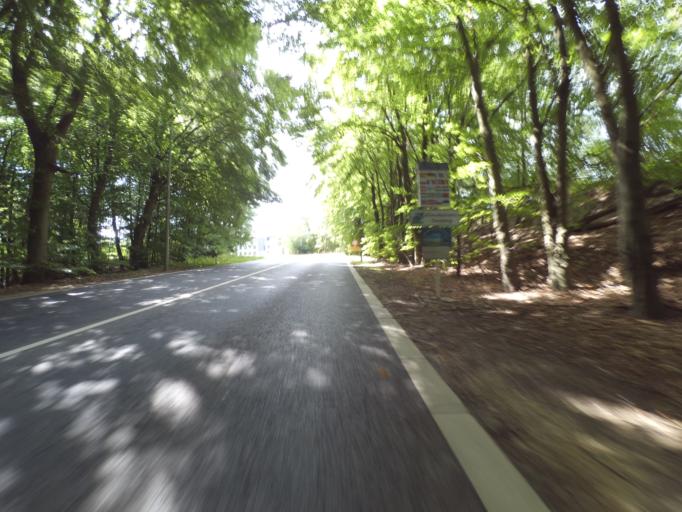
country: LU
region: Luxembourg
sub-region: Canton de Luxembourg
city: Niederanven
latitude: 49.6560
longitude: 6.2250
